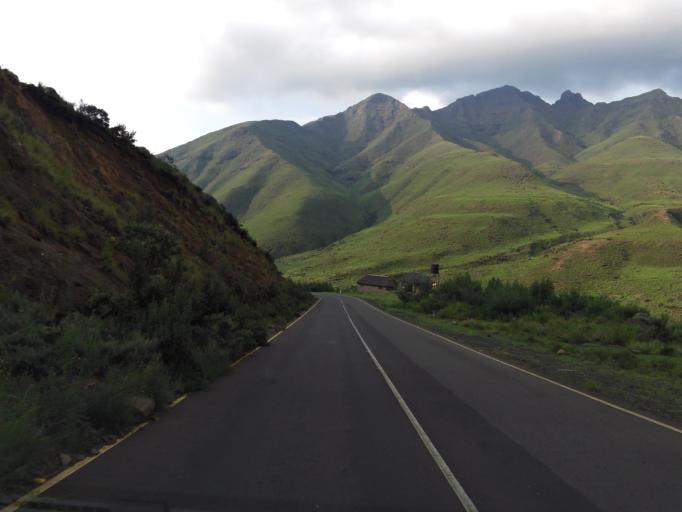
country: LS
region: Butha-Buthe
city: Butha-Buthe
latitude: -29.0537
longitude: 28.3453
